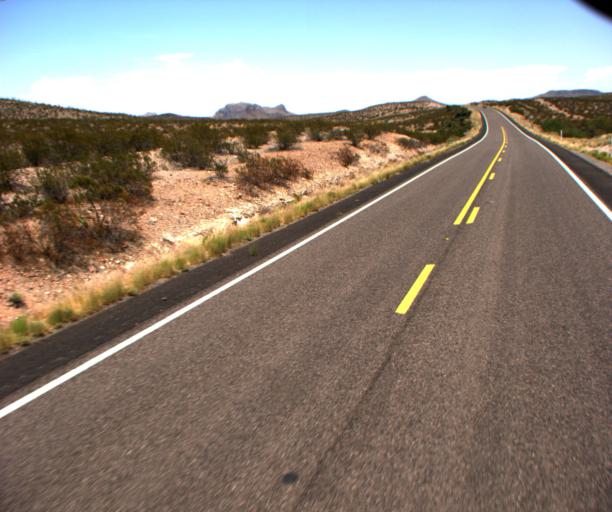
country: US
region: Arizona
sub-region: Greenlee County
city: Clifton
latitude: 32.7498
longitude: -109.3878
